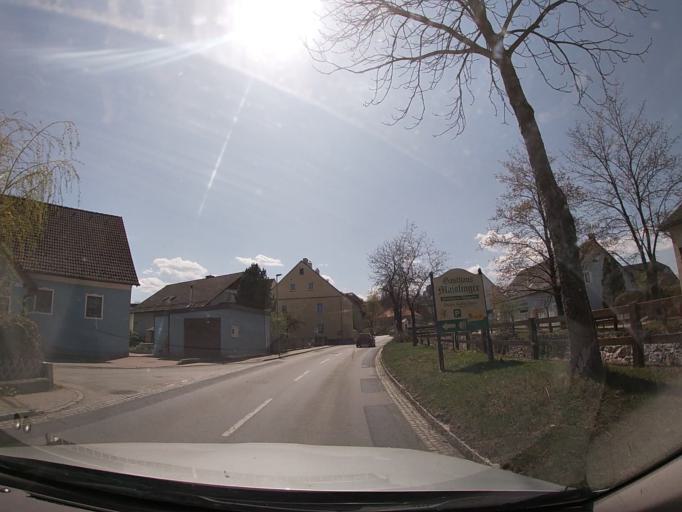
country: AT
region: Styria
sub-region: Politischer Bezirk Murtal
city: Grosslobming
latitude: 47.1853
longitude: 14.8094
